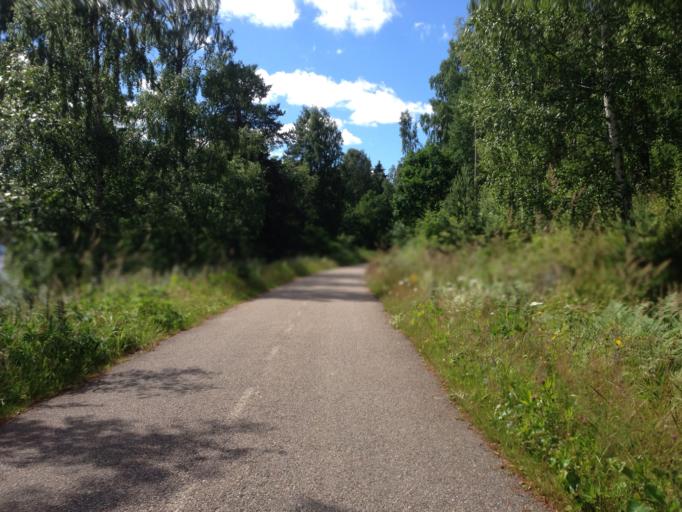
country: SE
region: Dalarna
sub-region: Ludvika Kommun
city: Ludvika
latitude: 60.1623
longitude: 15.1707
